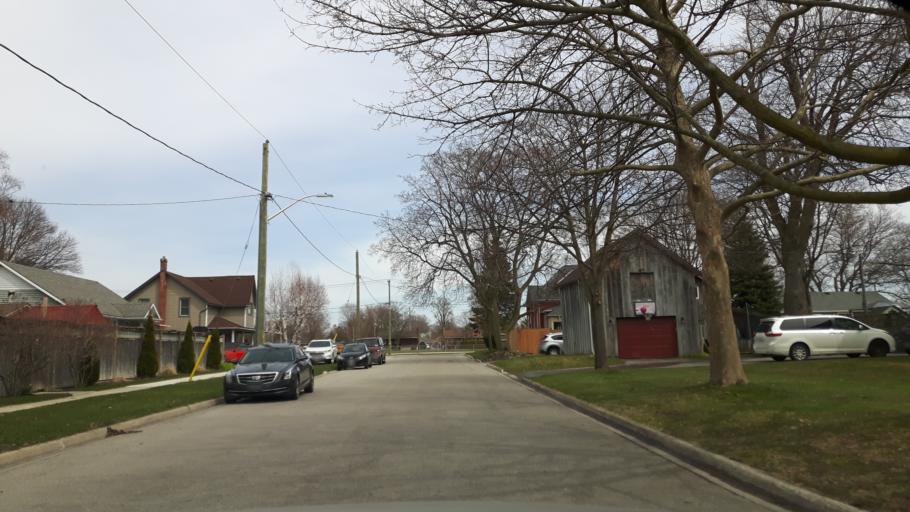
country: CA
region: Ontario
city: Goderich
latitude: 43.7371
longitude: -81.7098
